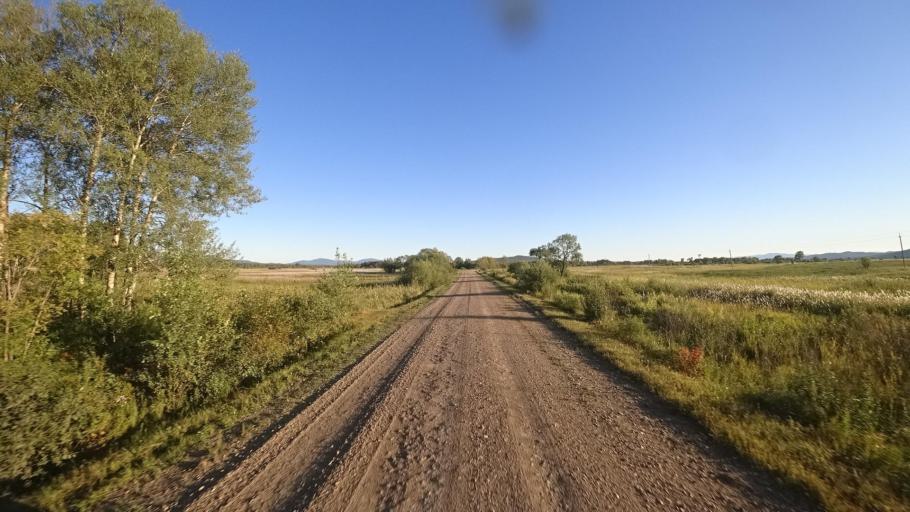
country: RU
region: Primorskiy
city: Kirovskiy
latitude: 44.7919
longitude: 133.6226
